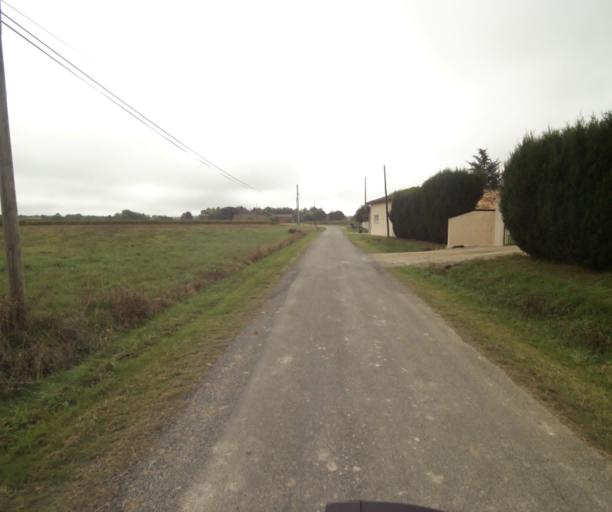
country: FR
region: Midi-Pyrenees
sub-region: Departement du Tarn-et-Garonne
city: Campsas
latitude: 43.8863
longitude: 1.3460
